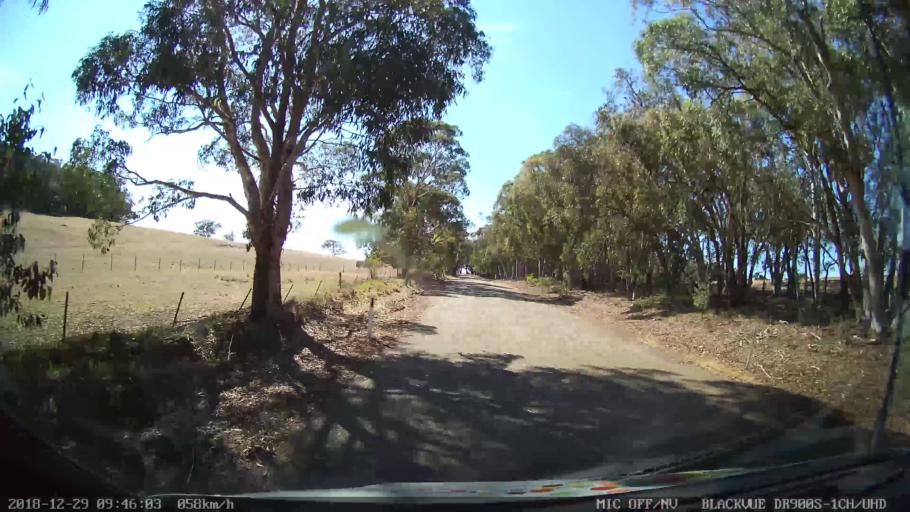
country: AU
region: New South Wales
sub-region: Upper Lachlan Shire
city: Crookwell
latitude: -34.6997
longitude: 149.4406
